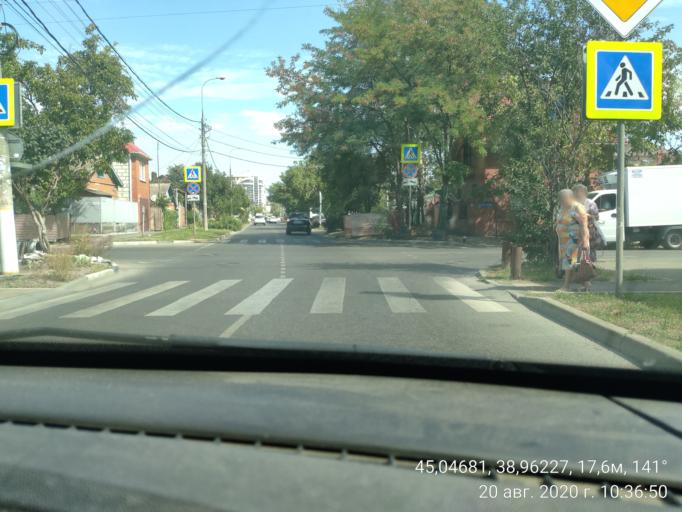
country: RU
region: Krasnodarskiy
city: Krasnodar
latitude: 45.0468
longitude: 38.9623
